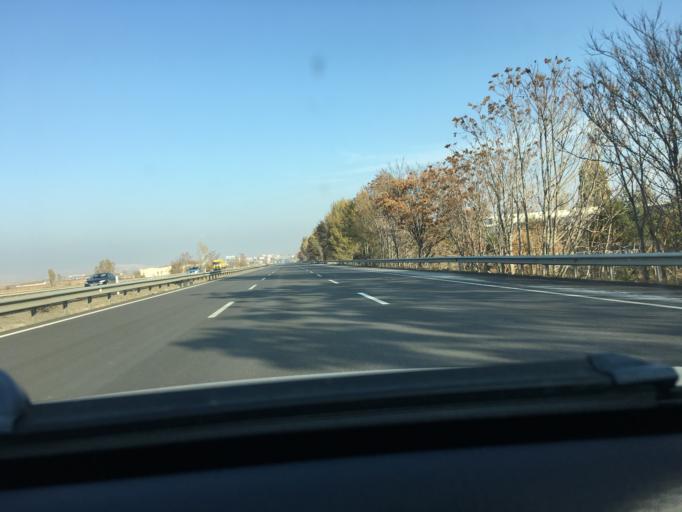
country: TR
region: Ankara
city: Temelli
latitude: 39.7159
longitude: 32.3075
